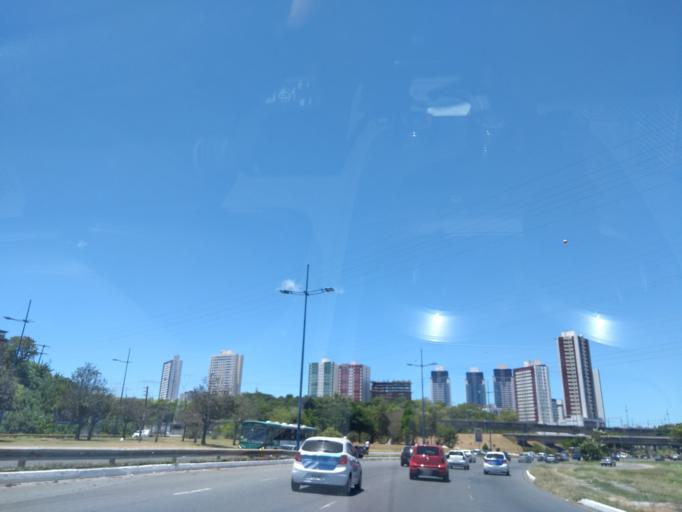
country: BR
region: Bahia
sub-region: Salvador
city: Salvador
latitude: -12.9770
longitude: -38.4753
